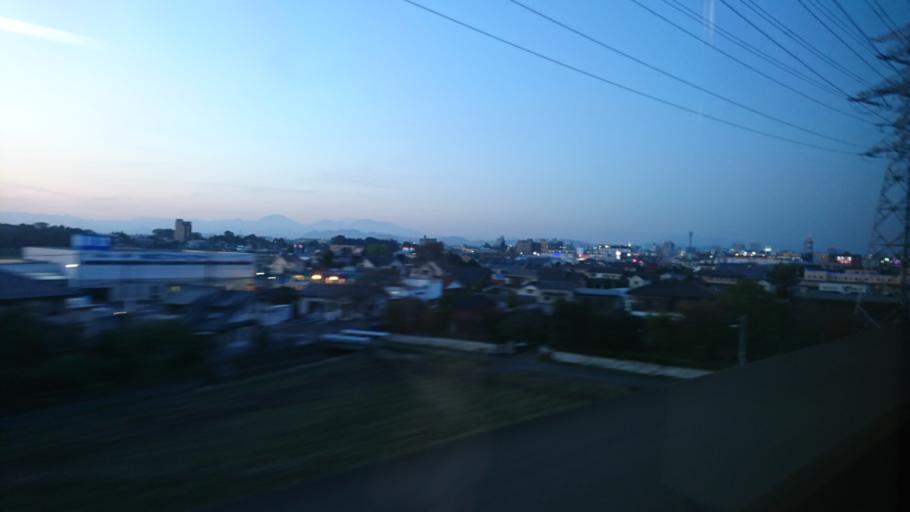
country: JP
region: Tochigi
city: Utsunomiya-shi
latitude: 36.5310
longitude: 139.8914
